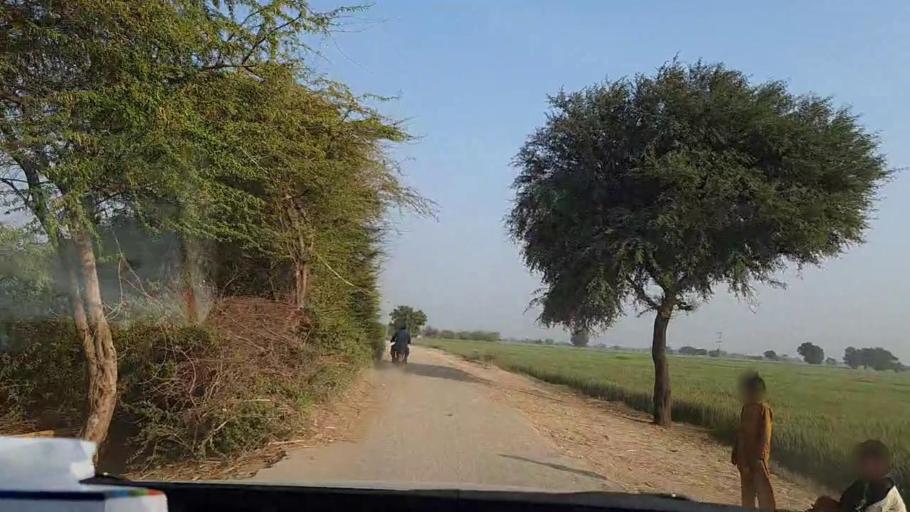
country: PK
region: Sindh
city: Tando Ghulam Ali
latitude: 25.2127
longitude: 68.8874
